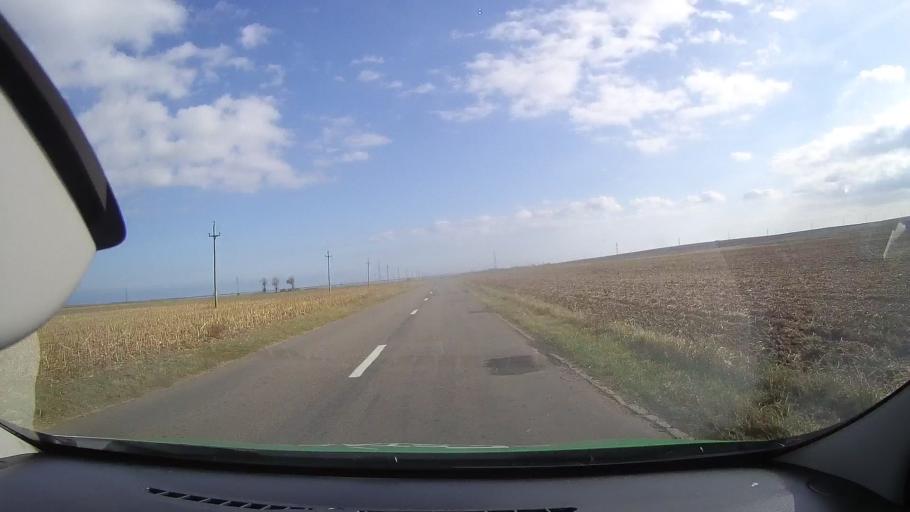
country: RO
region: Constanta
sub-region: Comuna Istria
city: Nuntasi
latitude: 44.5314
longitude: 28.6748
